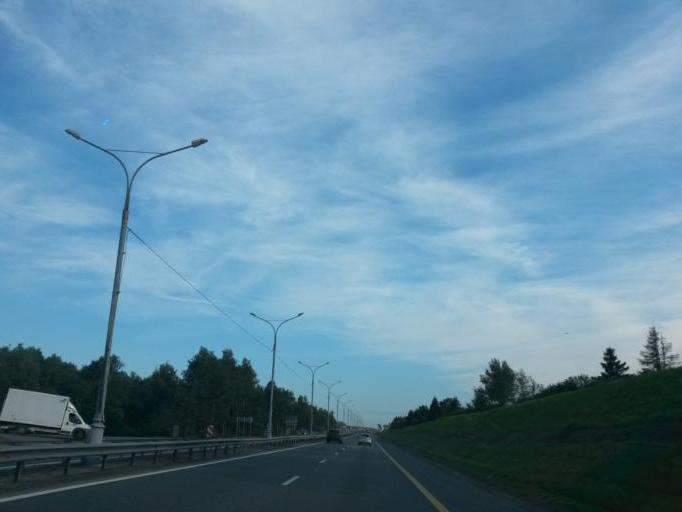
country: RU
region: Moskovskaya
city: Gorki-Leninskiye
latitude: 55.4798
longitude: 37.8516
